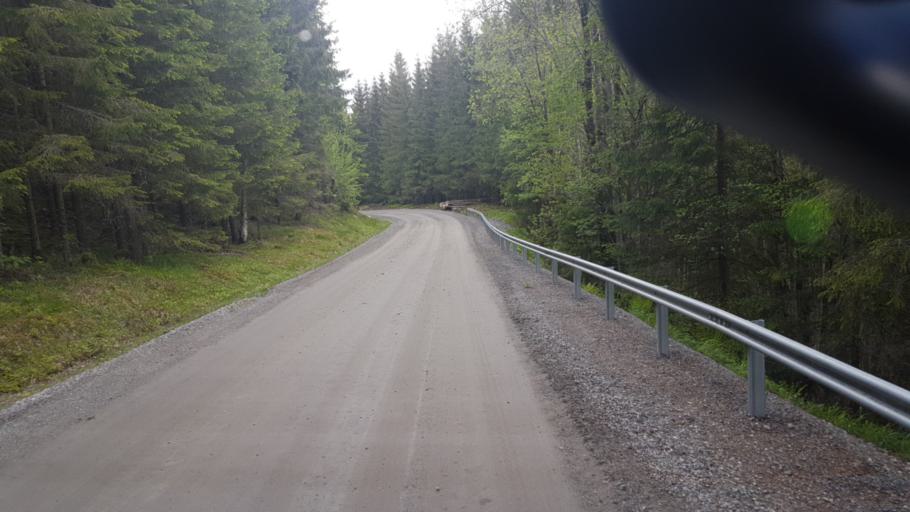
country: NO
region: Ostfold
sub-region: Romskog
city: Romskog
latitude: 59.7124
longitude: 11.9825
